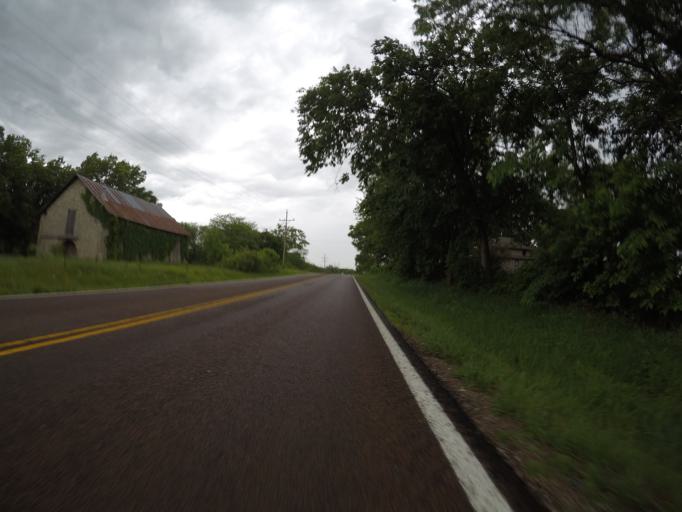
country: US
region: Kansas
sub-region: Shawnee County
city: Rossville
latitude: 38.9574
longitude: -96.0683
